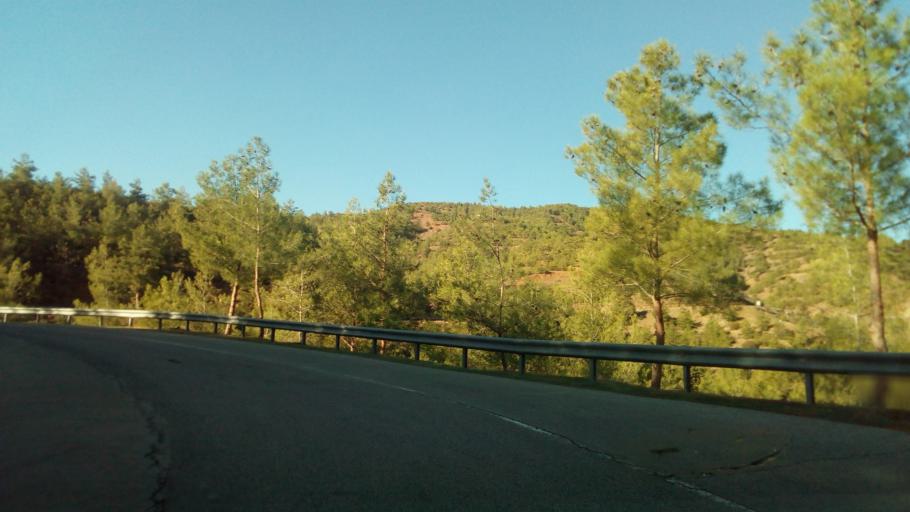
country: CY
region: Lefkosia
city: Lefka
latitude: 35.0862
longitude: 32.7854
